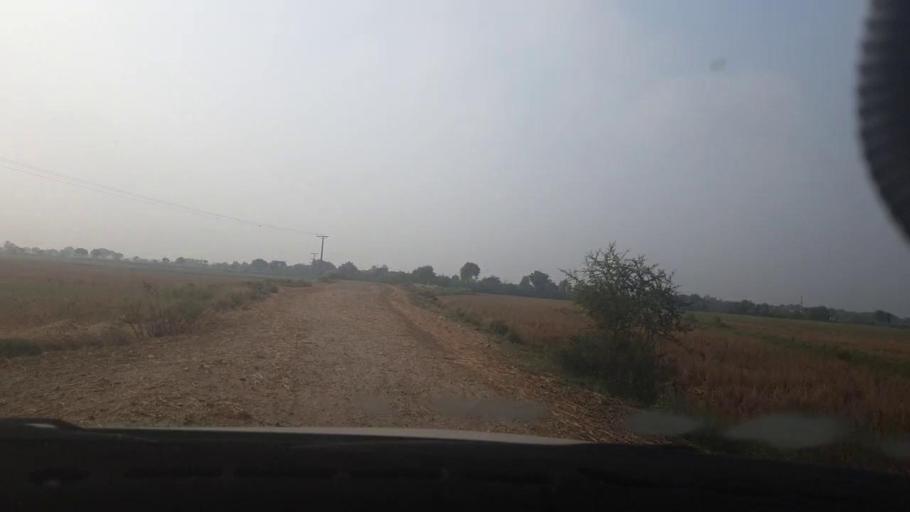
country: PK
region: Sindh
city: Tando Muhammad Khan
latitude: 25.0817
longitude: 68.5130
